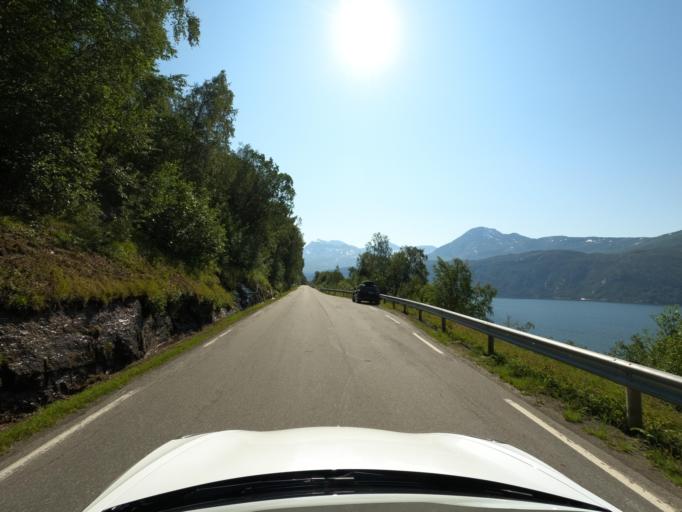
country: NO
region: Nordland
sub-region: Narvik
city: Narvik
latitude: 68.3469
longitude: 17.2797
